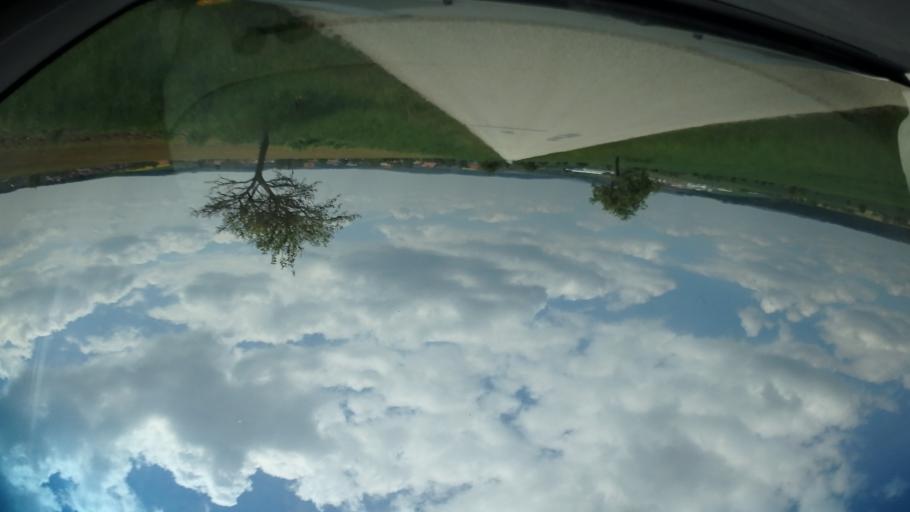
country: CZ
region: Vysocina
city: Mohelno
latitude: 49.1203
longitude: 16.1813
